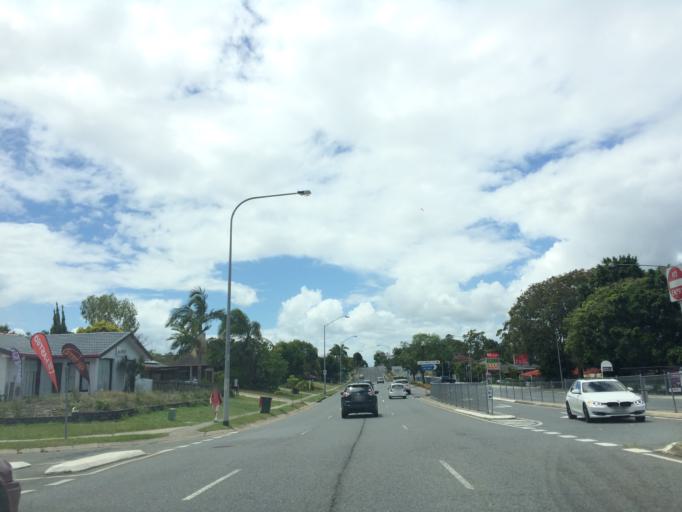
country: AU
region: Queensland
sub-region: Brisbane
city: Sunnybank Hills
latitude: -27.6104
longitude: 153.0543
